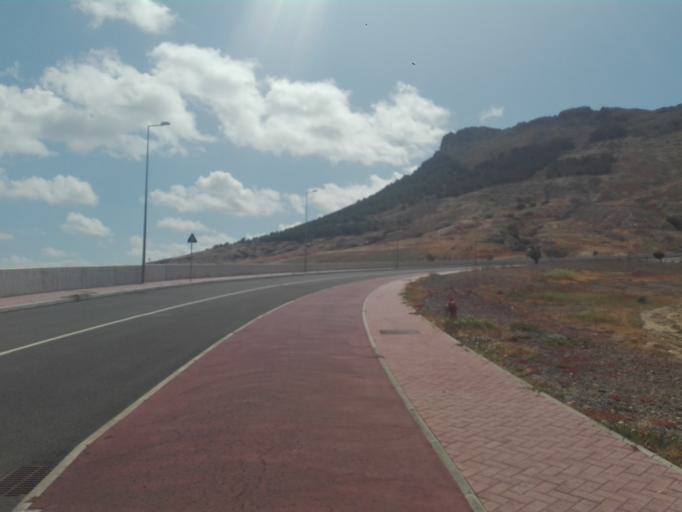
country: PT
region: Madeira
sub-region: Porto Santo
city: Vila de Porto Santo
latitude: 33.0462
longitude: -16.3622
